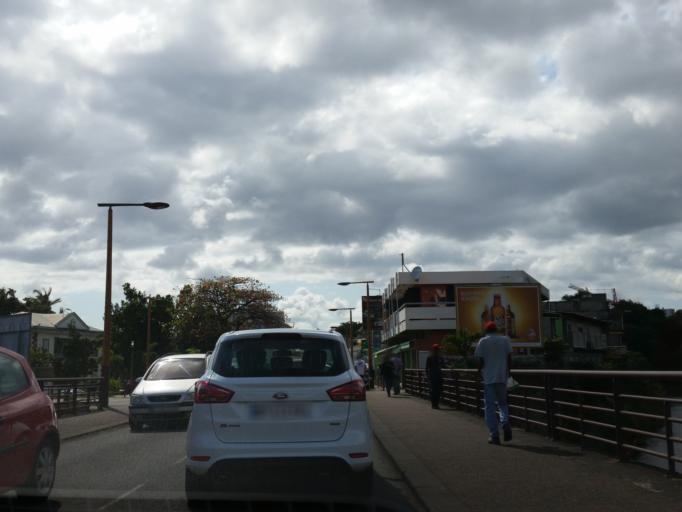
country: RE
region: Reunion
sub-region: Reunion
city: Sainte-Marie
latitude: -20.8976
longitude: 55.5485
